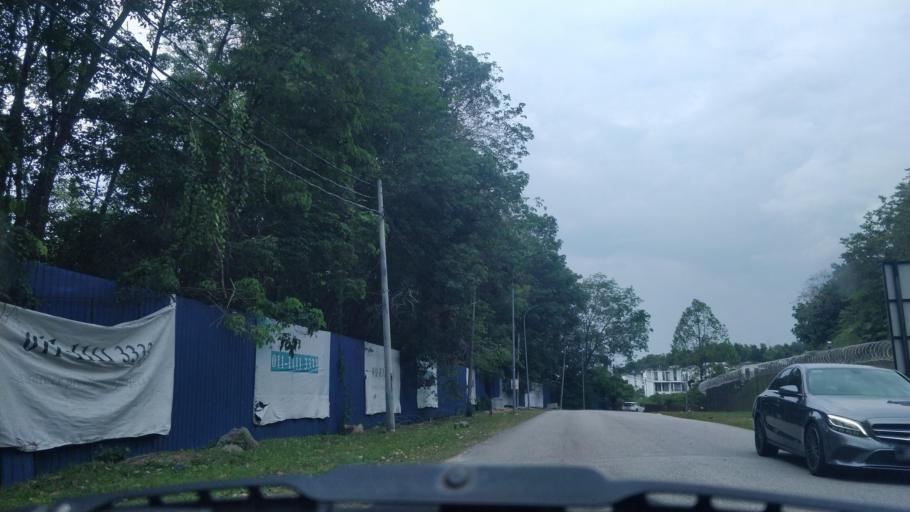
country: MY
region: Selangor
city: Kuang
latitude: 3.2062
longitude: 101.5857
